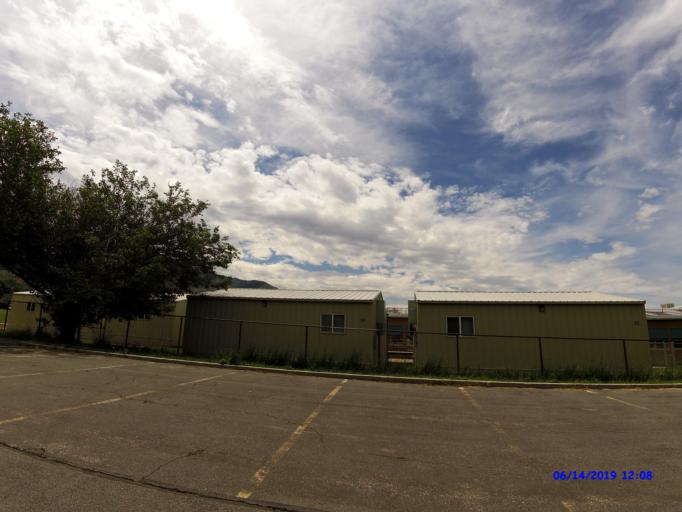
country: US
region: Utah
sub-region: Weber County
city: Ogden
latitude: 41.2497
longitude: -111.9448
